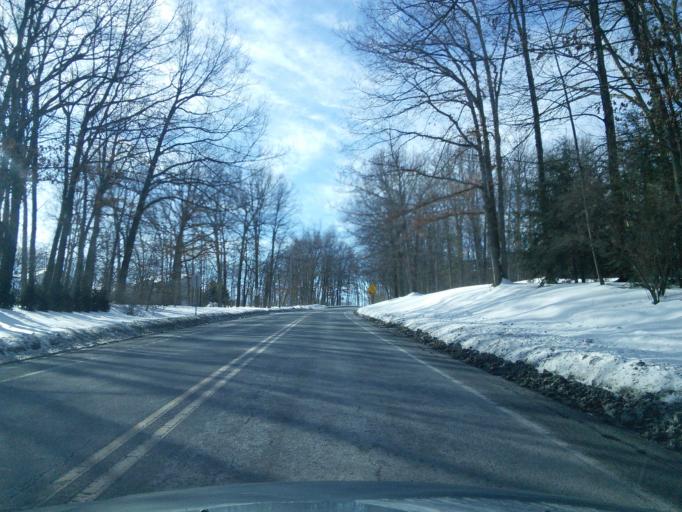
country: US
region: Pennsylvania
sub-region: Centre County
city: Park Forest Village
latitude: 40.8255
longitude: -77.8930
